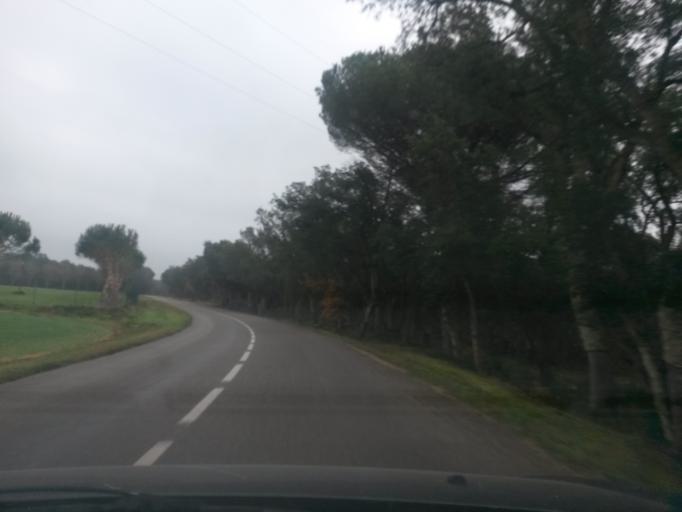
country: ES
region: Catalonia
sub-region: Provincia de Girona
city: Llagostera
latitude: 41.8361
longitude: 2.9328
